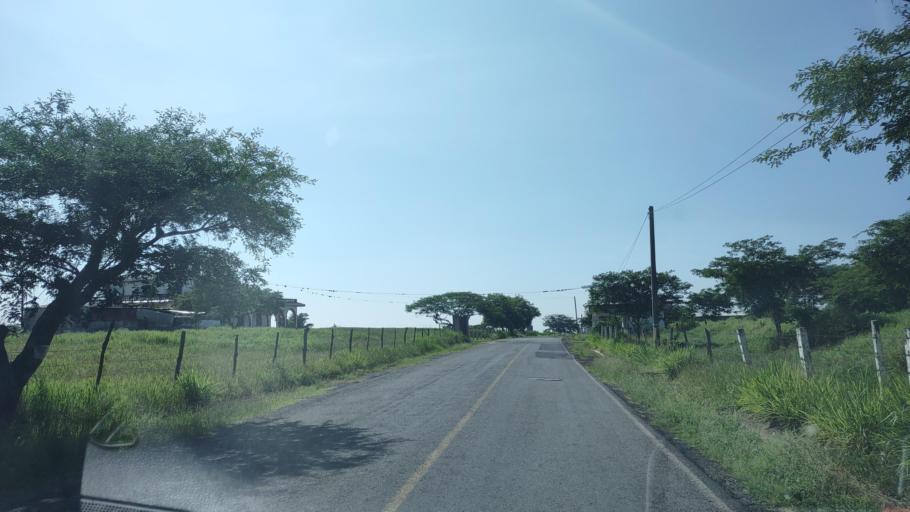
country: MX
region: Veracruz
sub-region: Emiliano Zapata
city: Jacarandas
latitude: 19.4946
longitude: -96.8253
